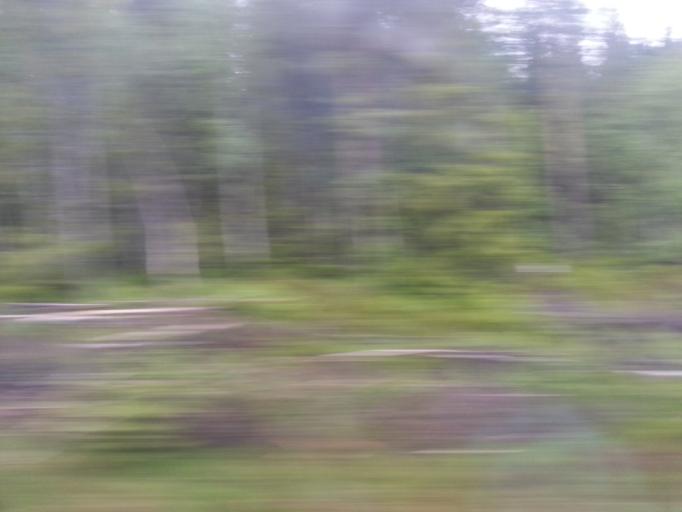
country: NO
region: Sor-Trondelag
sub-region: Rennebu
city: Berkak
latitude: 62.8092
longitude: 10.0357
